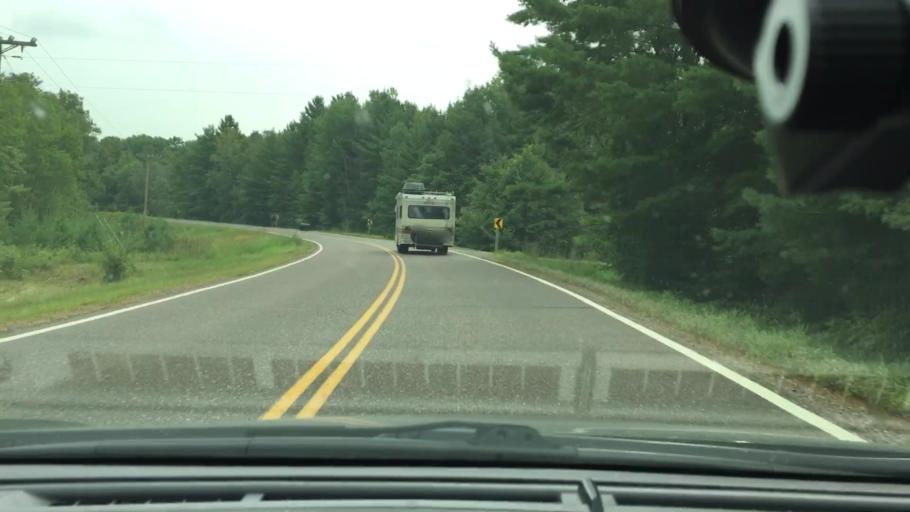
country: US
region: Minnesota
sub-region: Aitkin County
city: Aitkin
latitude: 46.4023
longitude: -93.8018
